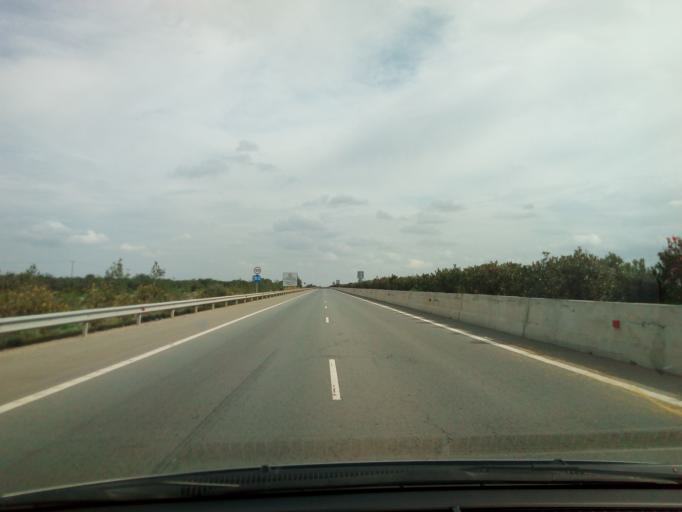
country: CY
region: Lefkosia
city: Kokkinotrimithia
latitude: 35.1617
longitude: 33.1691
